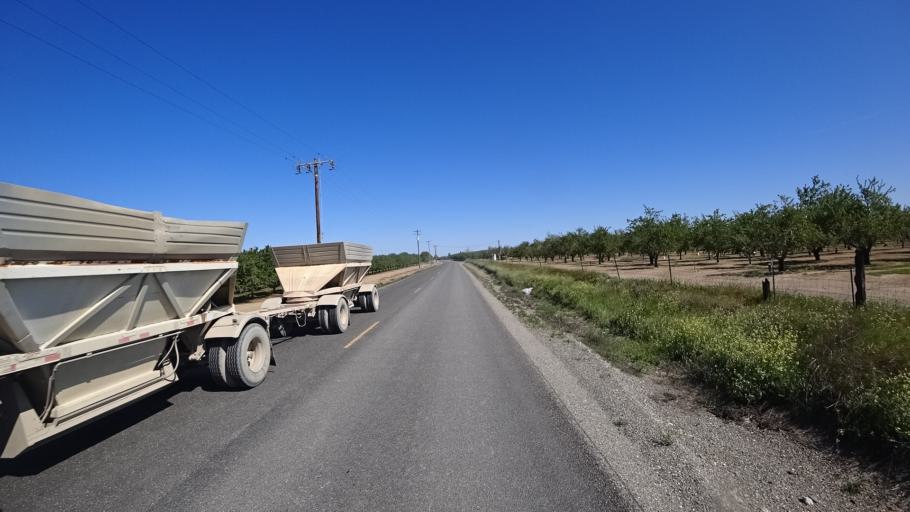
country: US
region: California
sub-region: Glenn County
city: Hamilton City
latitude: 39.6939
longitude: -122.1032
